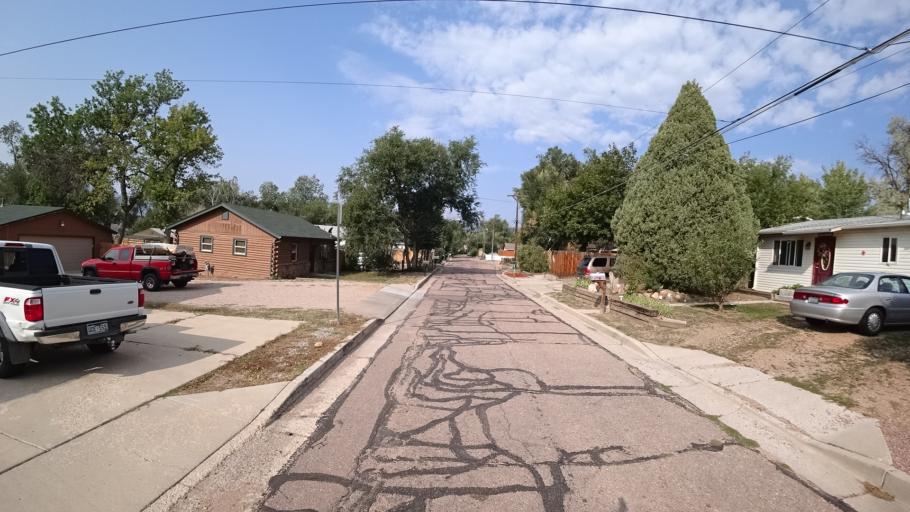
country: US
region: Colorado
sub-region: El Paso County
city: Colorado Springs
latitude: 38.8480
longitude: -104.7812
